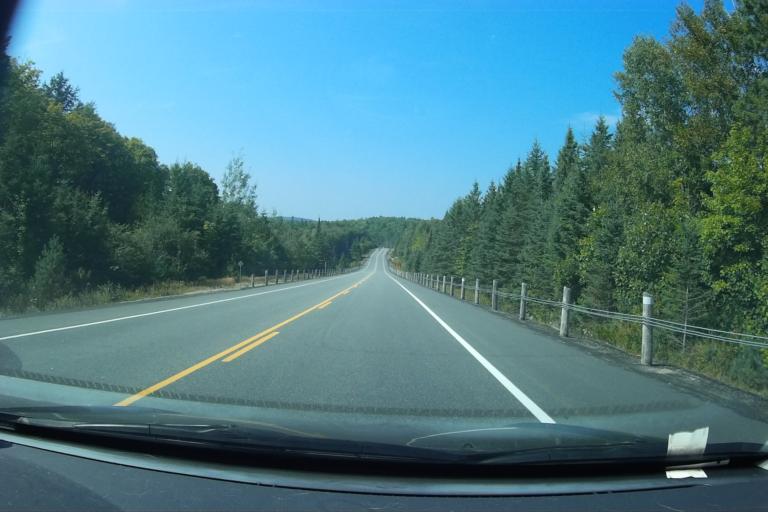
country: CA
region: Ontario
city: Huntsville
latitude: 45.5430
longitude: -78.6862
